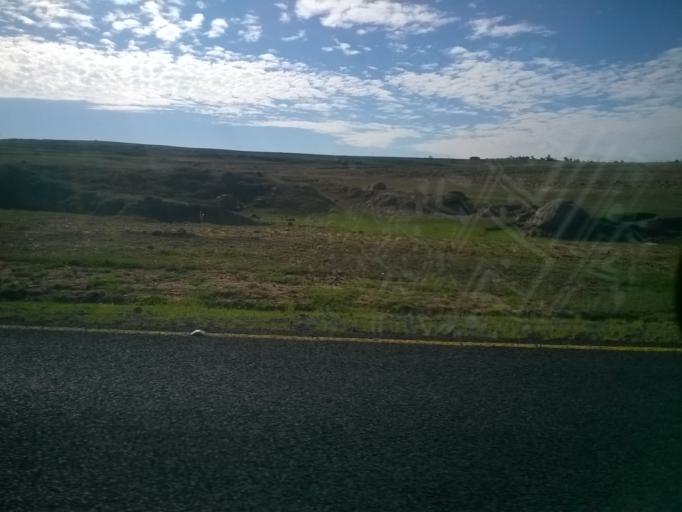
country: LS
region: Berea
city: Teyateyaneng
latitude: -29.0824
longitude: 27.8667
